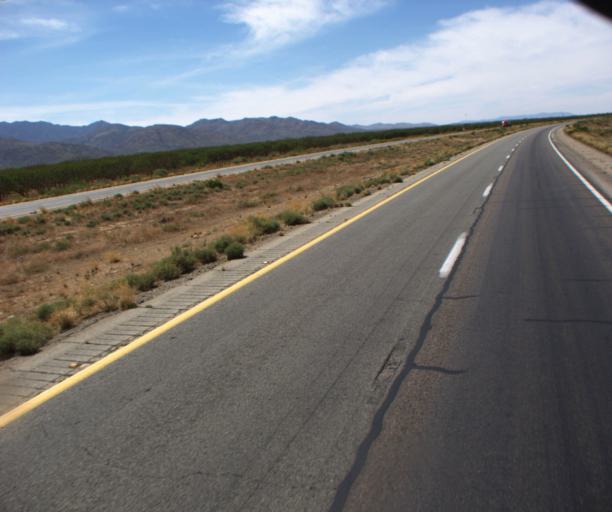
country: US
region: Arizona
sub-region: Cochise County
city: Willcox
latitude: 32.3177
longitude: -109.4880
